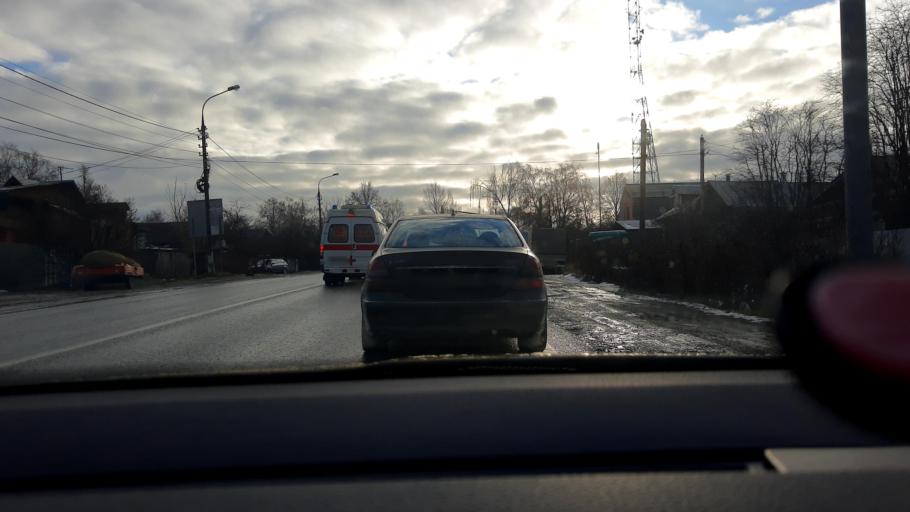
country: RU
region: Moskovskaya
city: Lesnyye Polyany
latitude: 55.9884
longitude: 37.8682
